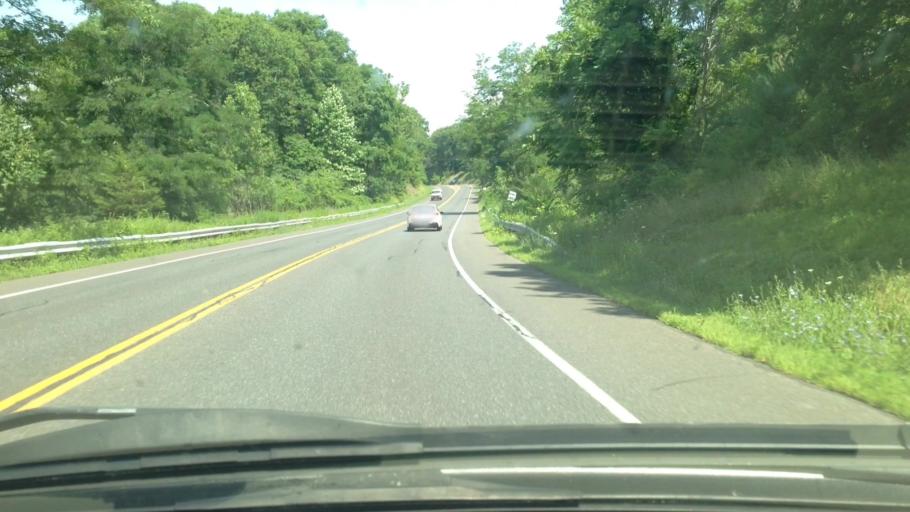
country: US
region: New York
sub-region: Ulster County
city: Lincoln Park
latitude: 41.9553
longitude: -73.9800
